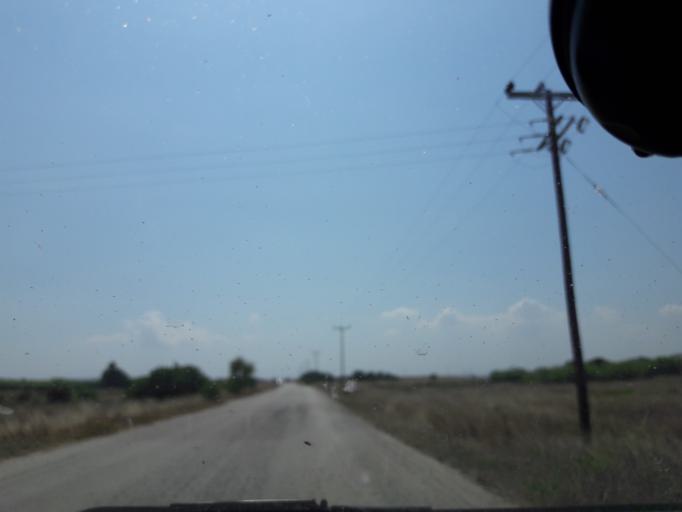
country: GR
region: North Aegean
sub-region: Nomos Lesvou
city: Myrina
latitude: 39.9047
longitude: 25.3038
